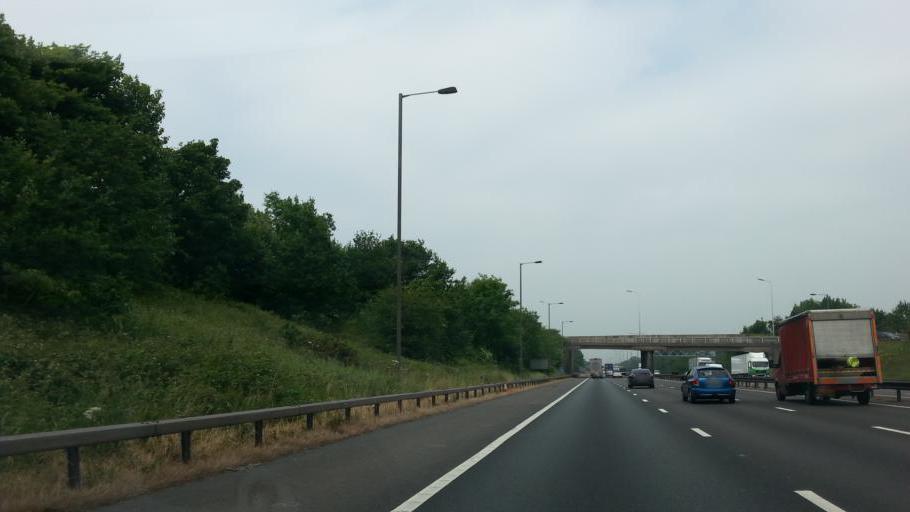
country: GB
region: England
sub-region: Staffordshire
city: Essington
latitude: 52.6352
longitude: -2.0523
